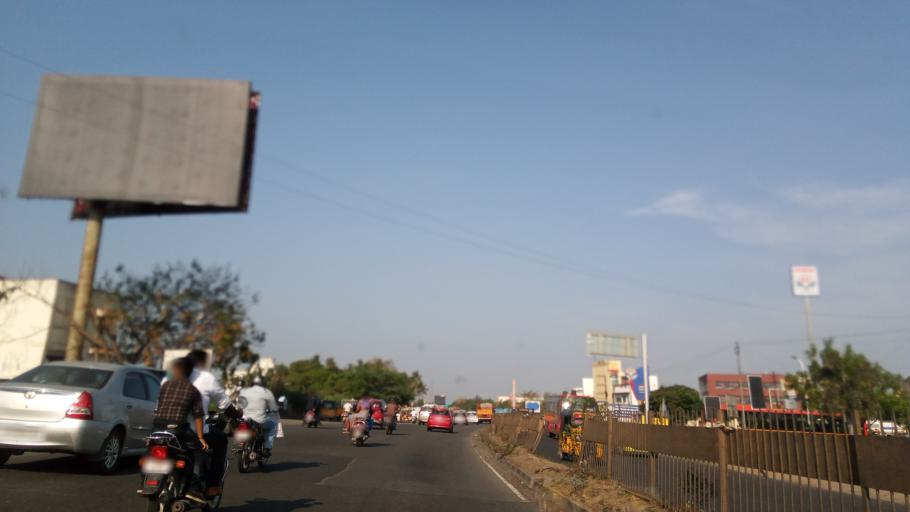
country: IN
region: Tamil Nadu
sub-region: Kancheepuram
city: Poonamalle
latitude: 13.0459
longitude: 80.0712
